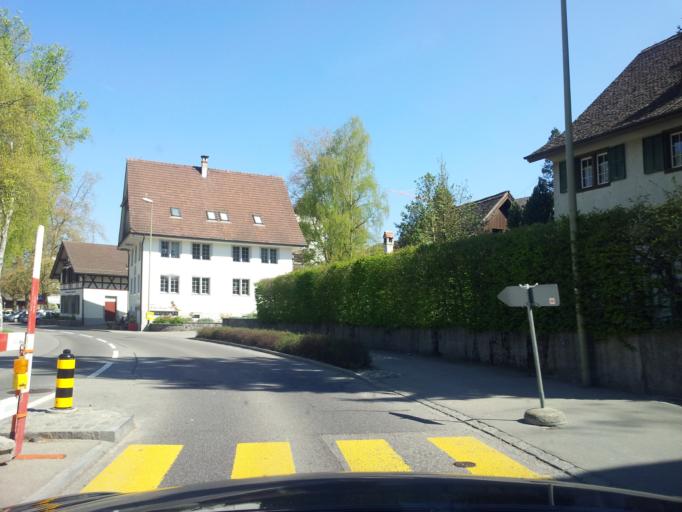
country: CH
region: Zurich
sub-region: Bezirk Affoltern
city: Affoltern am Albis
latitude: 47.2779
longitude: 8.4544
